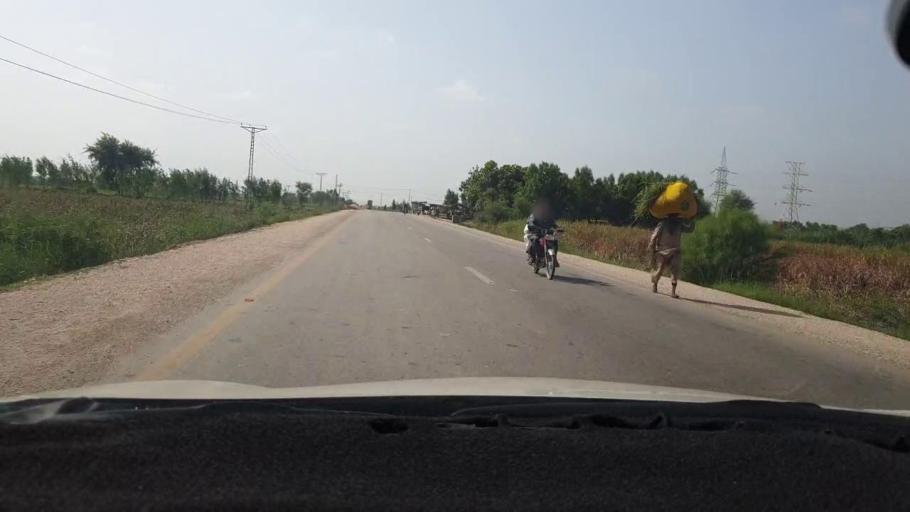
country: PK
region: Sindh
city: Tando Mittha Khan
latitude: 25.7884
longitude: 69.0714
